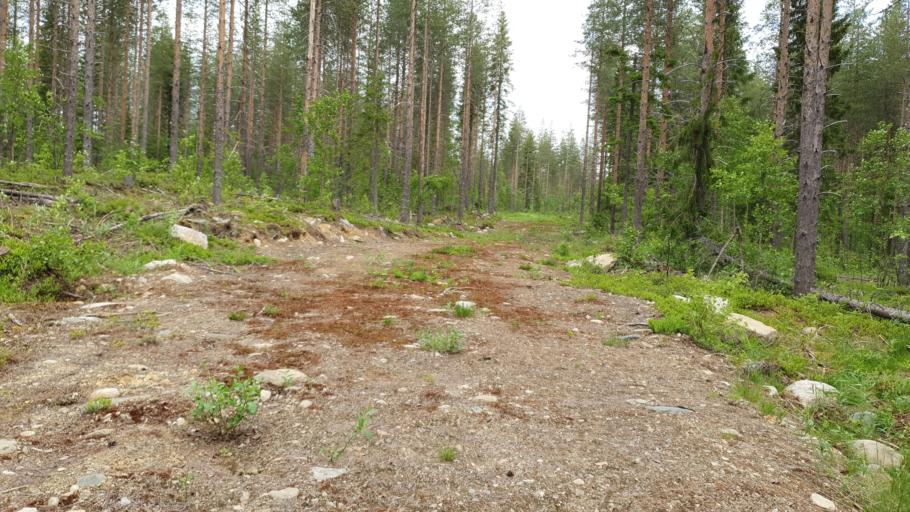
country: FI
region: Kainuu
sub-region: Kehys-Kainuu
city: Kuhmo
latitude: 64.4446
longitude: 29.6831
